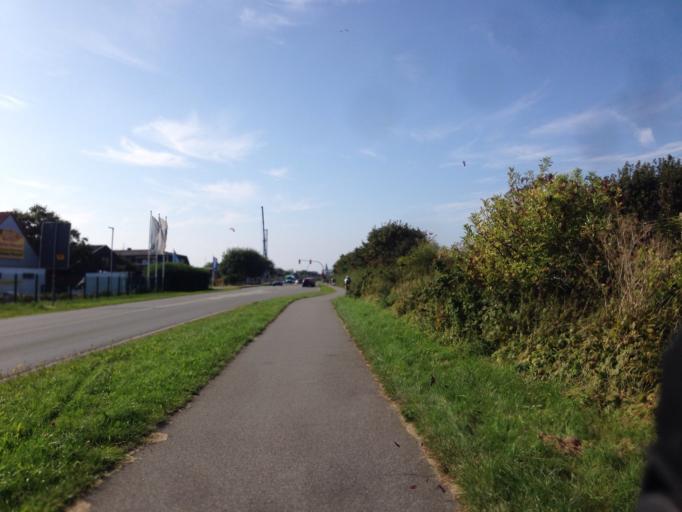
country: DE
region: Schleswig-Holstein
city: Tinnum
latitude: 54.9021
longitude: 8.3306
